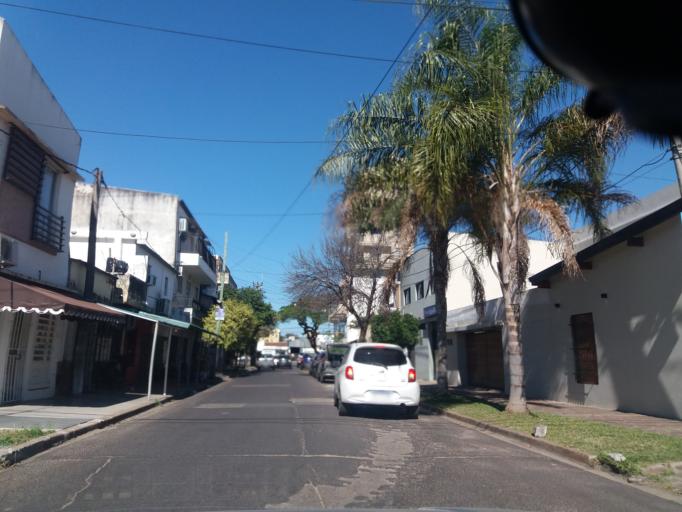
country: AR
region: Corrientes
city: Corrientes
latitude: -27.4737
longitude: -58.8447
